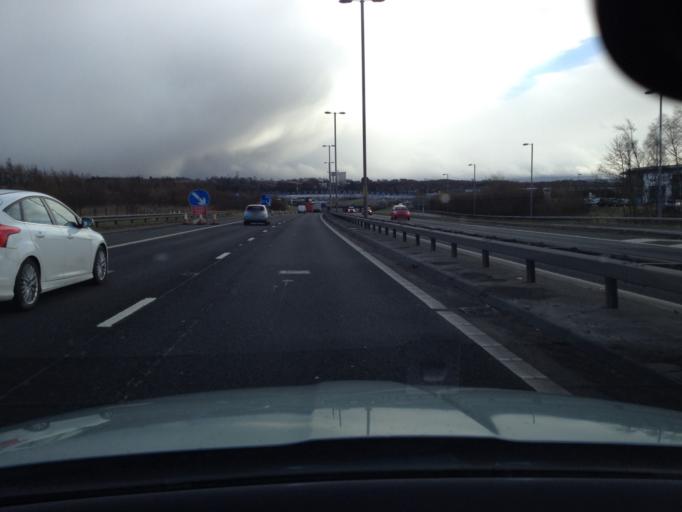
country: GB
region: Scotland
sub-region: Edinburgh
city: Kirkliston
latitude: 55.9433
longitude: -3.4046
